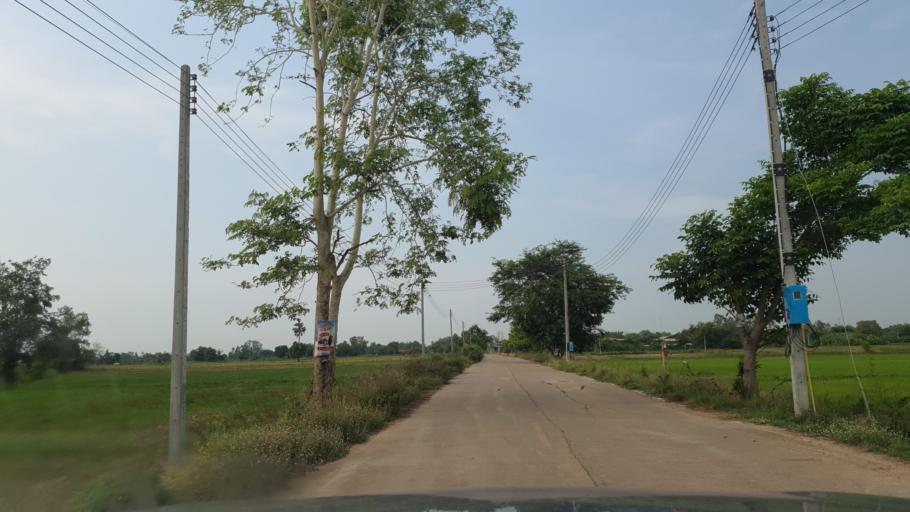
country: TH
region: Phitsanulok
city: Bang Rakam
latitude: 16.8025
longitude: 100.1629
